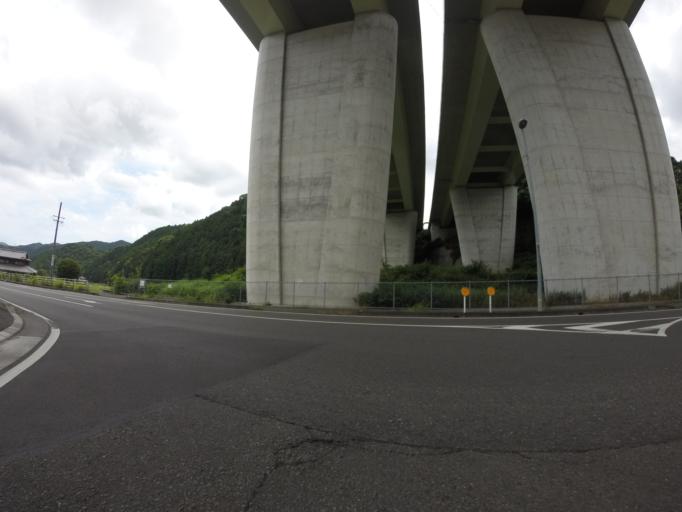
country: JP
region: Shizuoka
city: Shizuoka-shi
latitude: 34.9869
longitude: 138.2968
